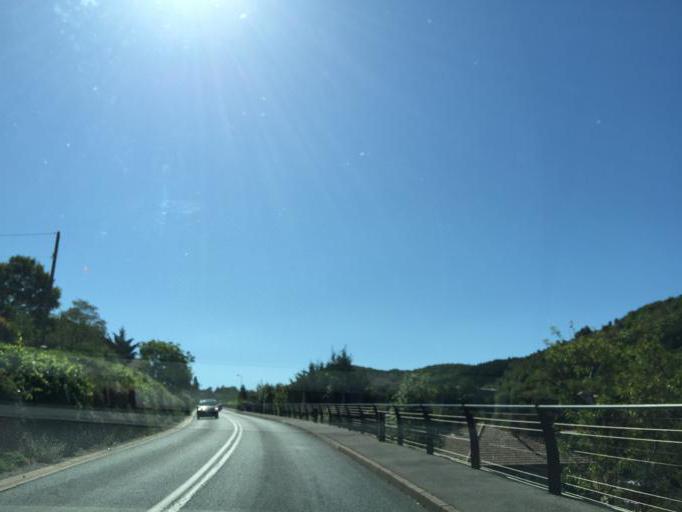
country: FR
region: Midi-Pyrenees
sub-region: Departement de l'Aveyron
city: Saint-Georges-de-Luzencon
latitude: 44.0471
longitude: 2.9007
